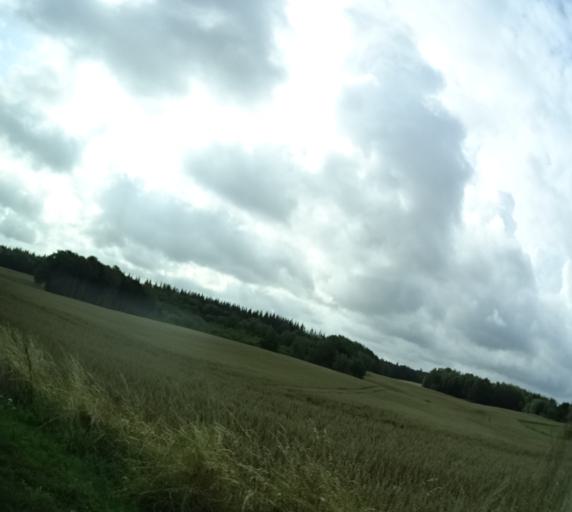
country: DK
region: Central Jutland
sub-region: Syddjurs Kommune
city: Ryomgard
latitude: 56.4025
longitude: 10.5071
